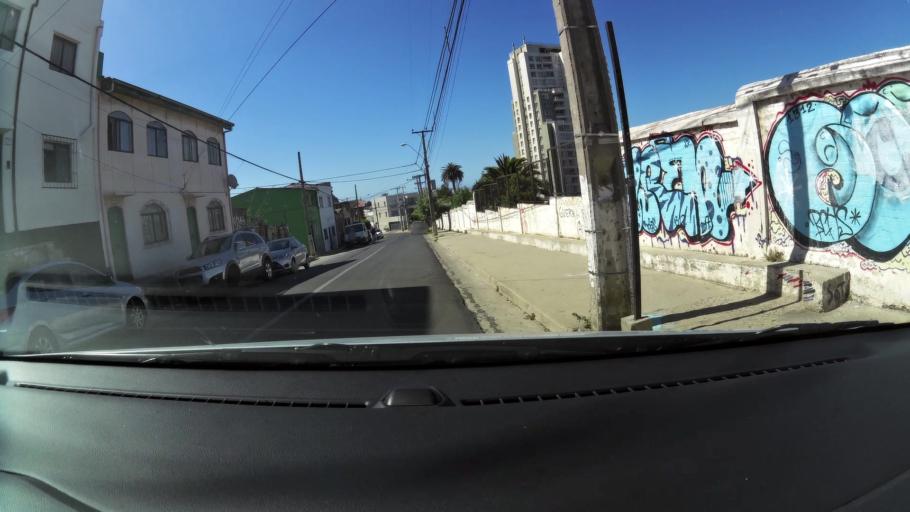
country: CL
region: Valparaiso
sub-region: Provincia de Valparaiso
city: Valparaiso
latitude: -33.0244
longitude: -71.6336
